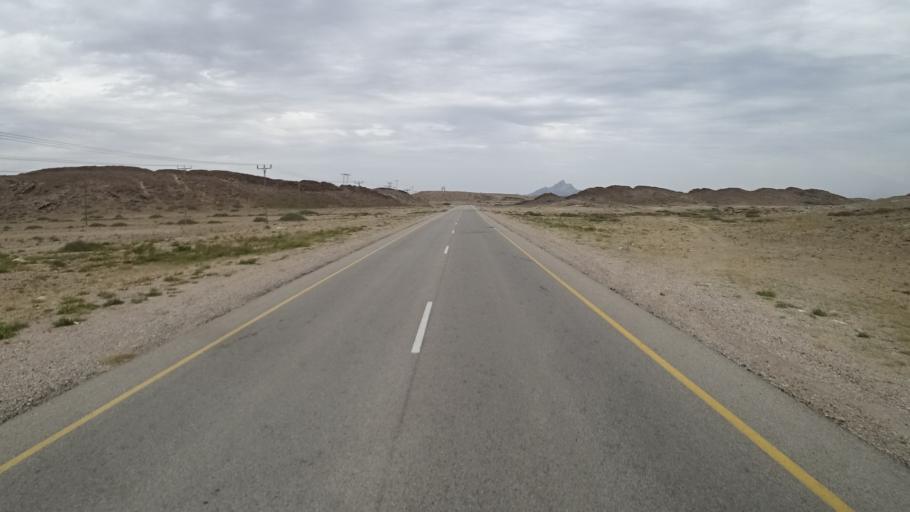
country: OM
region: Zufar
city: Salalah
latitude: 17.0685
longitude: 54.8843
